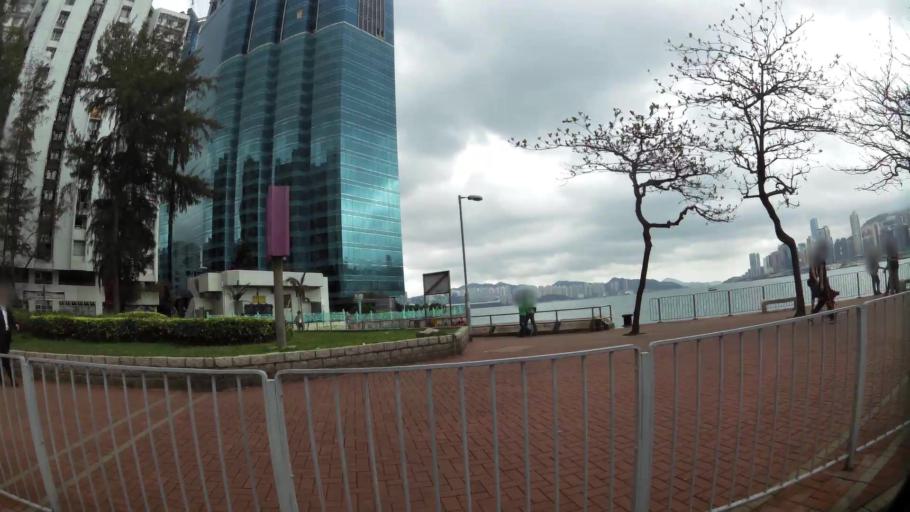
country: HK
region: Kowloon City
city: Kowloon
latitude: 22.3017
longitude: 114.1908
